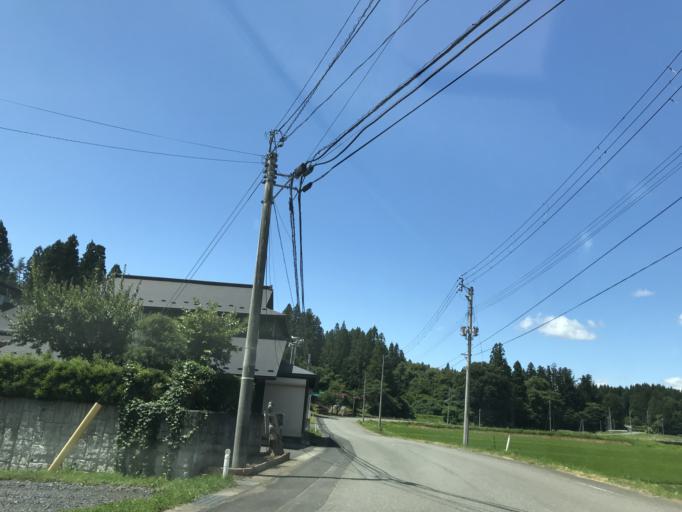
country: JP
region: Iwate
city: Ichinoseki
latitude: 38.9306
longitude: 141.0176
